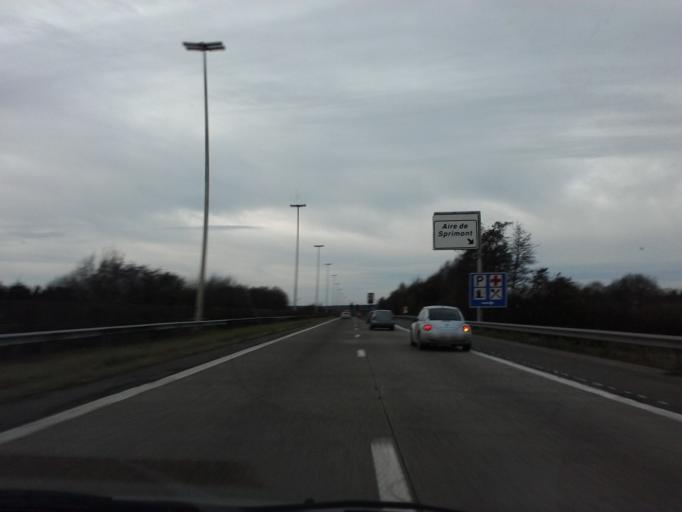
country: BE
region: Wallonia
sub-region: Province de Liege
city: Sprimont
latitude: 50.5188
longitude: 5.6727
